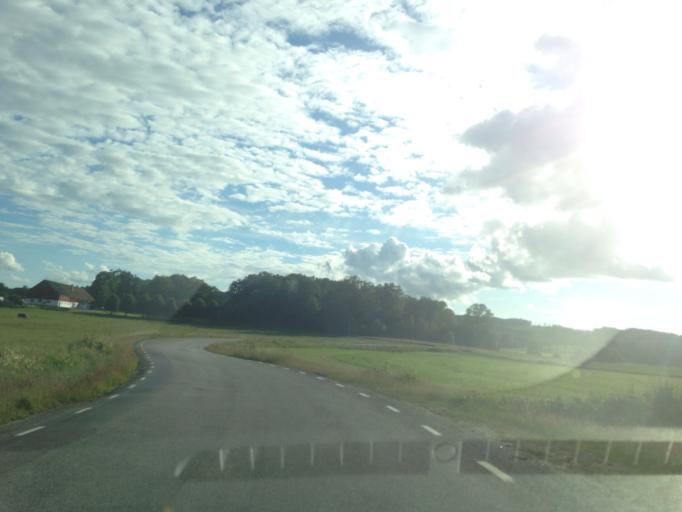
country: SE
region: Vaestra Goetaland
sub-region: Marks Kommun
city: Horred
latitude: 57.4718
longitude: 12.4637
